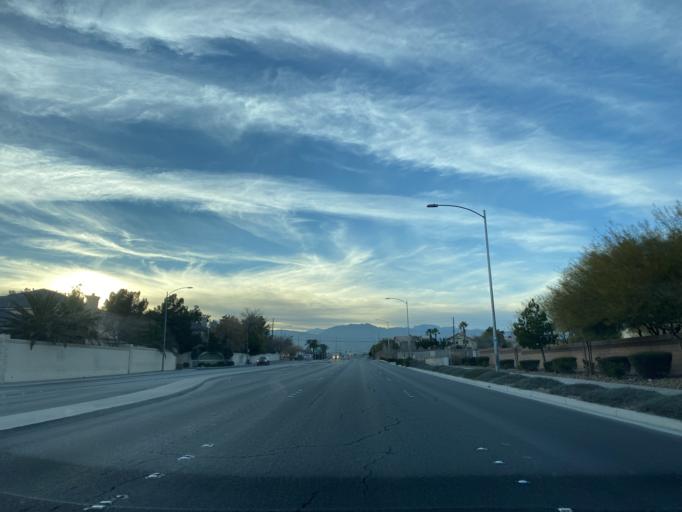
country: US
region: Nevada
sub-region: Clark County
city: Las Vegas
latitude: 36.2633
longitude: -115.2452
